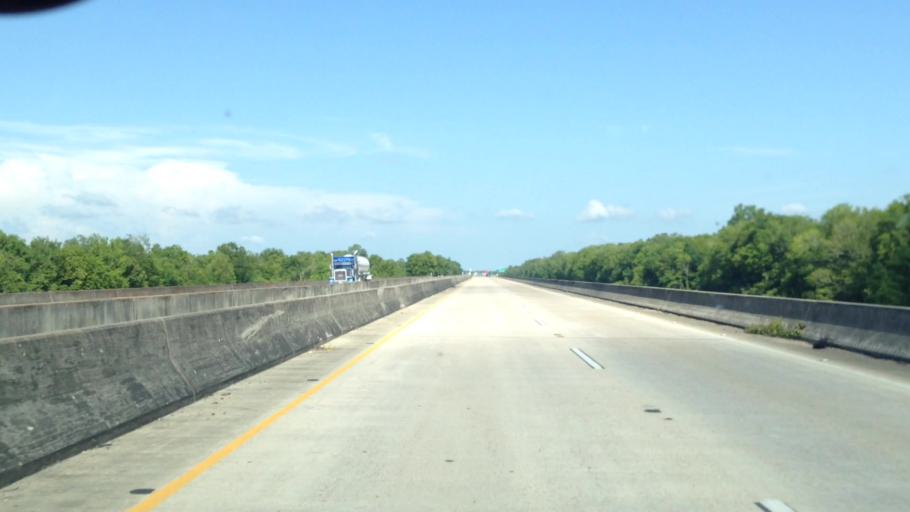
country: US
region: Louisiana
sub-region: Saint Landry Parish
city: Krotz Springs
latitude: 30.5424
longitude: -91.7906
